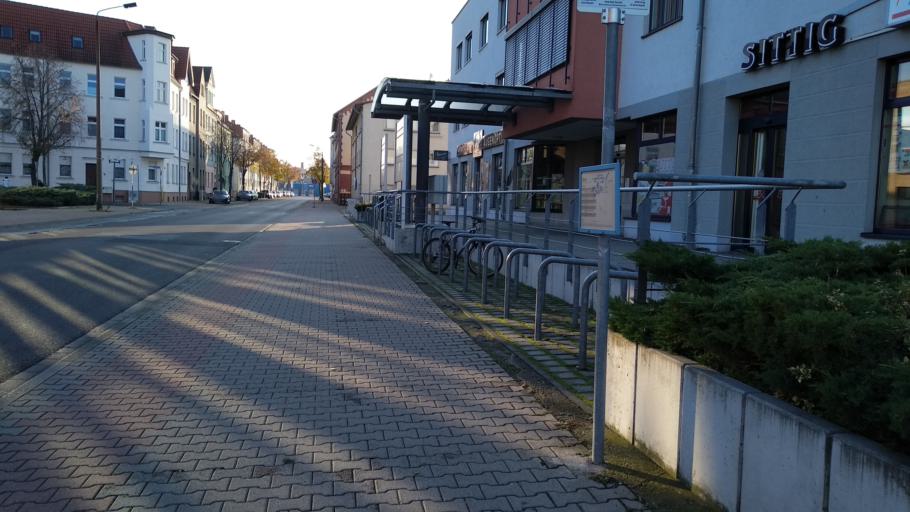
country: DE
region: Saxony
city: Bitterfeld-Wolfen
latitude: 51.6212
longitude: 12.3180
